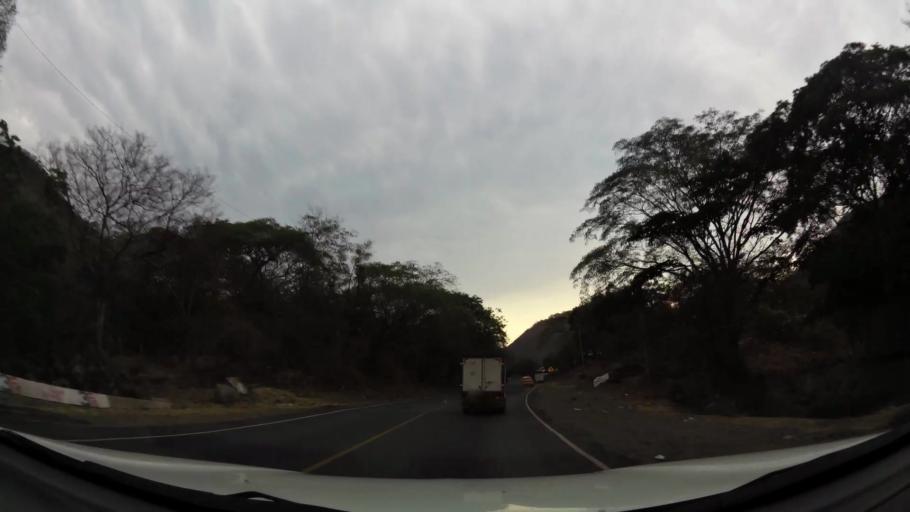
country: NI
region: Esteli
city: Esteli
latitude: 12.9489
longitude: -86.2230
